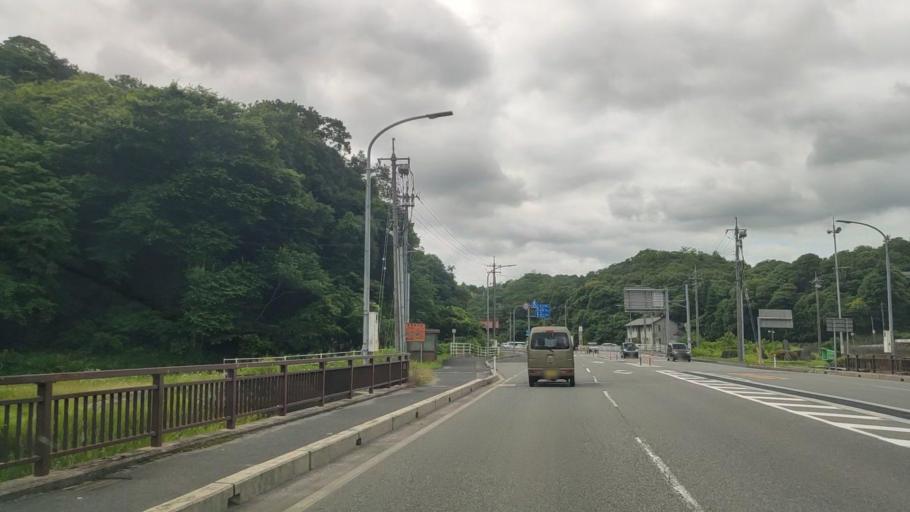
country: JP
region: Tottori
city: Yonago
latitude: 35.4157
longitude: 133.3530
